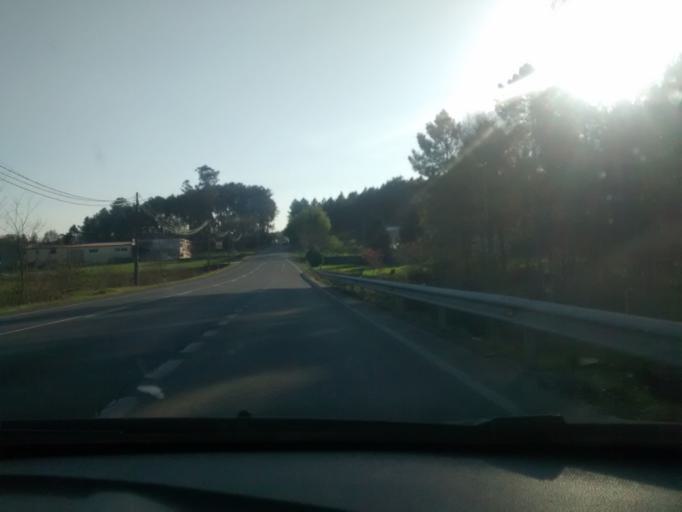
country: ES
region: Galicia
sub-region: Provincia de Pontevedra
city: A Estrada
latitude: 42.6977
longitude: -8.4594
